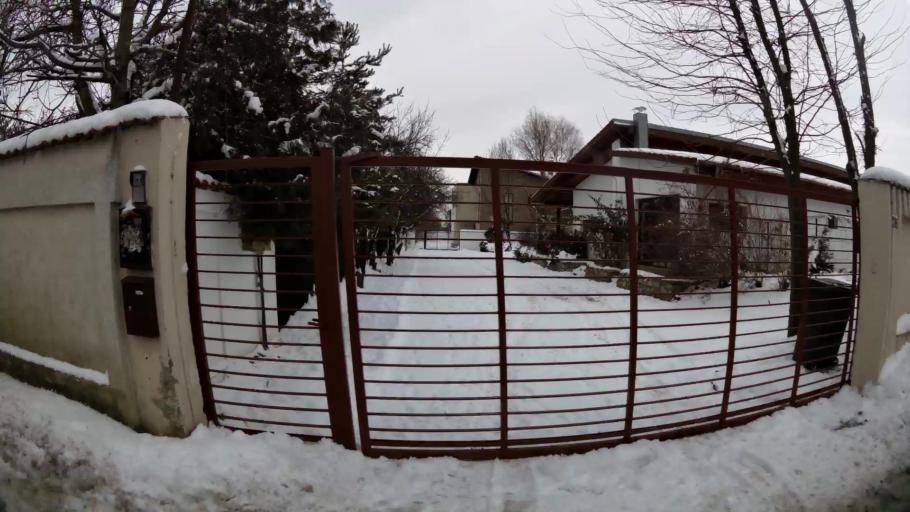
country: RO
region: Ilfov
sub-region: Comuna Tunari
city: Tunari
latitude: 44.5108
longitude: 26.1101
